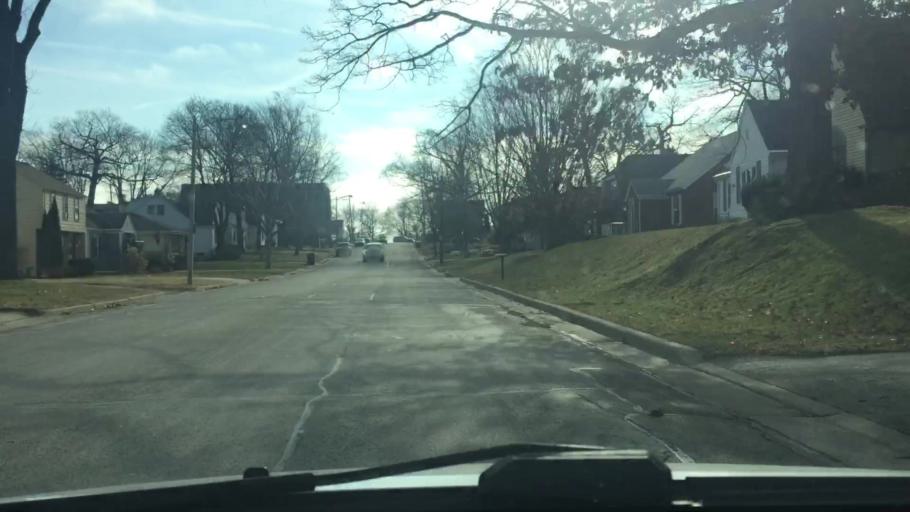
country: US
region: Wisconsin
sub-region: Waukesha County
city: Elm Grove
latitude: 43.0378
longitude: -88.0562
